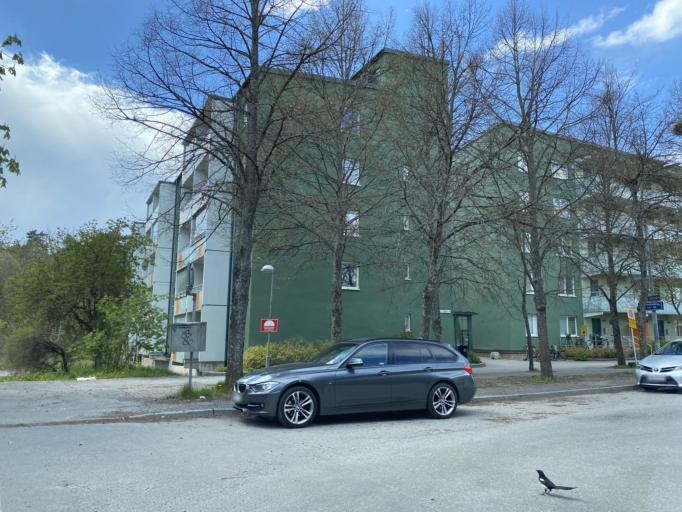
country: SE
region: Stockholm
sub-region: Stockholms Kommun
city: Kista
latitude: 59.4087
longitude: 17.9215
